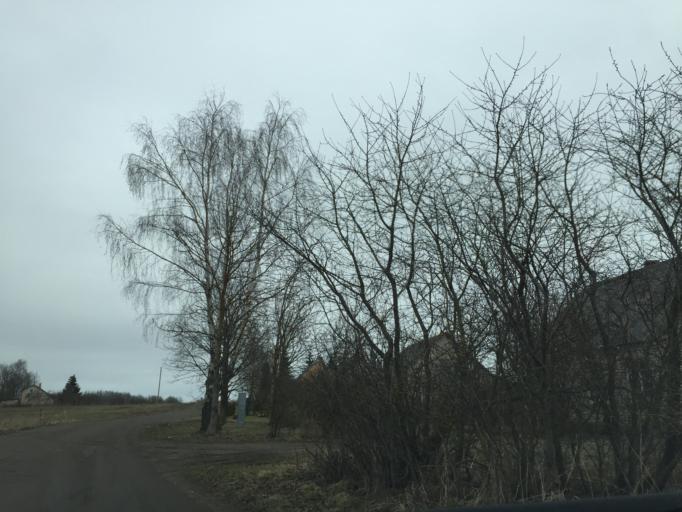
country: LV
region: Daugavpils
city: Daugavpils
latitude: 55.9190
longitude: 26.7405
